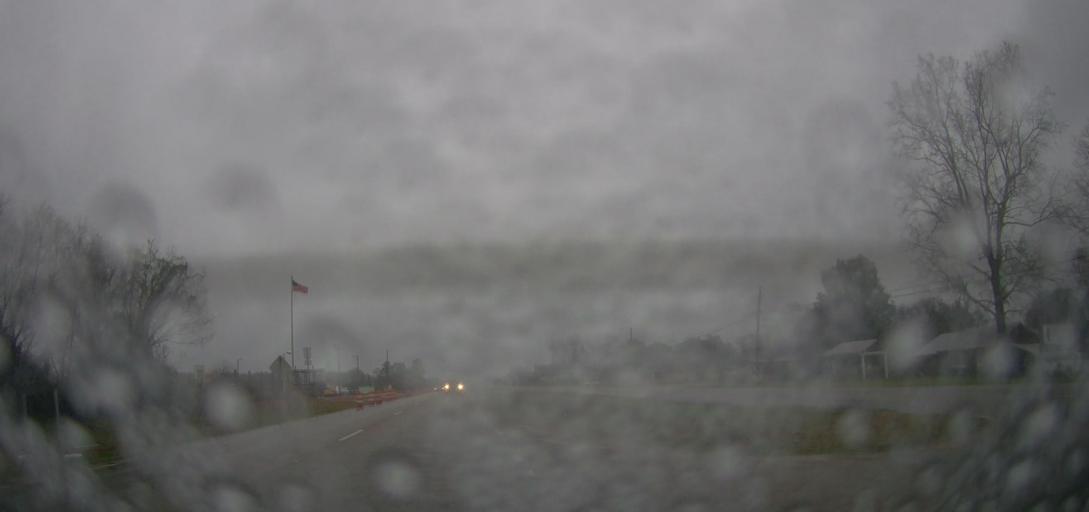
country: US
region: Alabama
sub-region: Autauga County
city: Prattville
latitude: 32.4374
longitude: -86.4244
